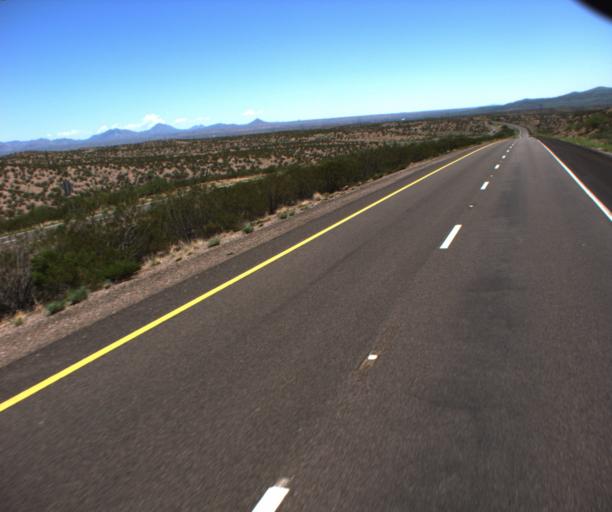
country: US
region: Arizona
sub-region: Greenlee County
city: Clifton
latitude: 33.0019
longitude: -109.2778
